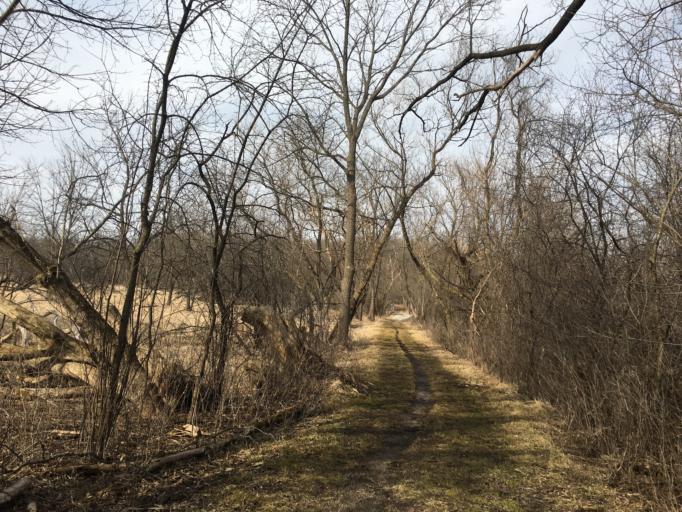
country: US
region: Illinois
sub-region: Cook County
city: Streamwood
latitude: 42.0460
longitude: -88.1983
